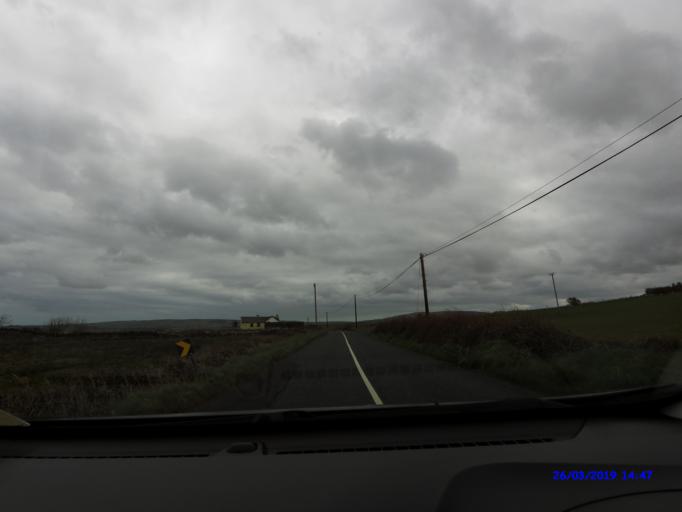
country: IE
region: Connaught
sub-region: Maigh Eo
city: Crossmolina
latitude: 54.3026
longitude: -9.4091
